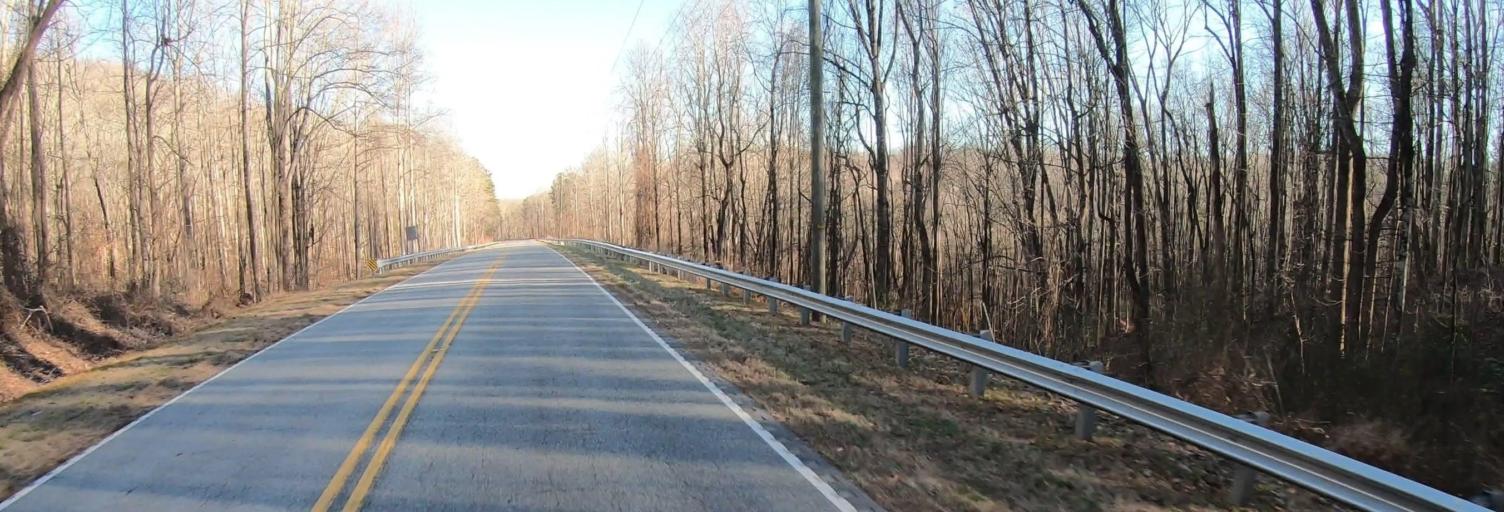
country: US
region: South Carolina
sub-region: Greenville County
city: Tigerville
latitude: 35.1034
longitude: -82.3812
